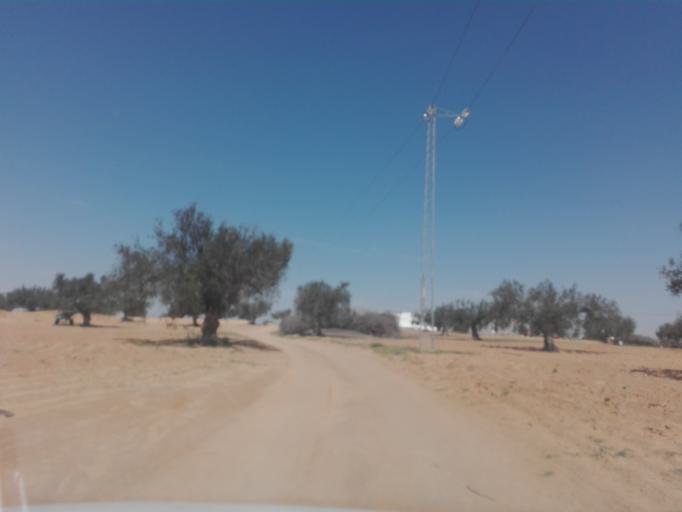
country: TN
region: Safaqis
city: Bi'r `Ali Bin Khalifah
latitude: 34.6636
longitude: 10.3083
